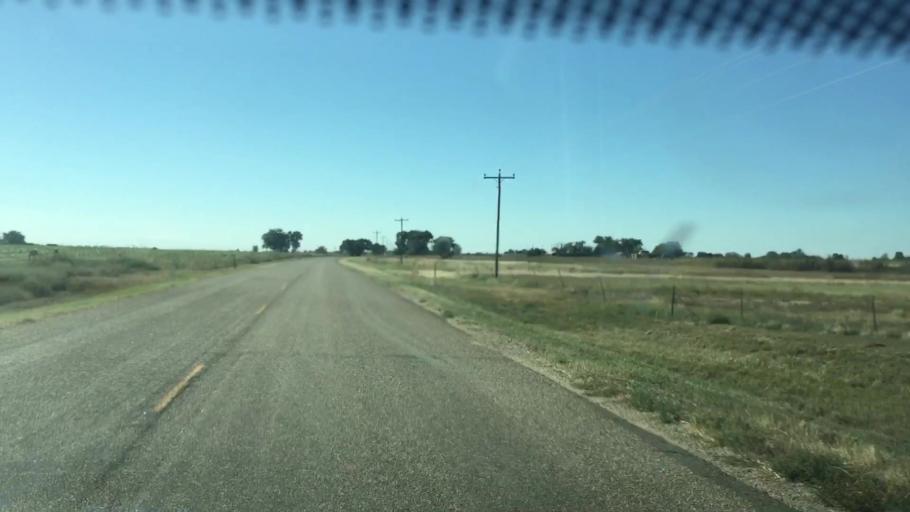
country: US
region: Colorado
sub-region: Prowers County
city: Lamar
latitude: 38.1146
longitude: -102.5769
